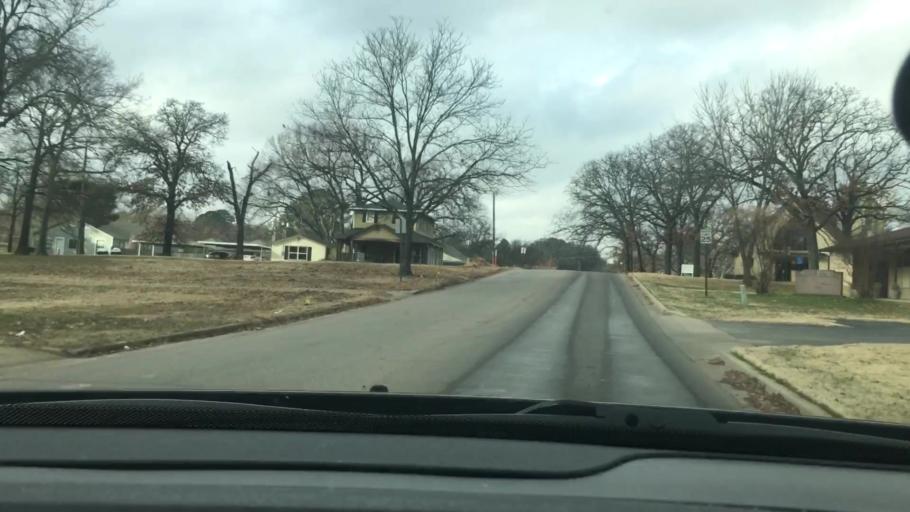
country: US
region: Oklahoma
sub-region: Bryan County
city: Durant
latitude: 34.0050
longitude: -96.3804
